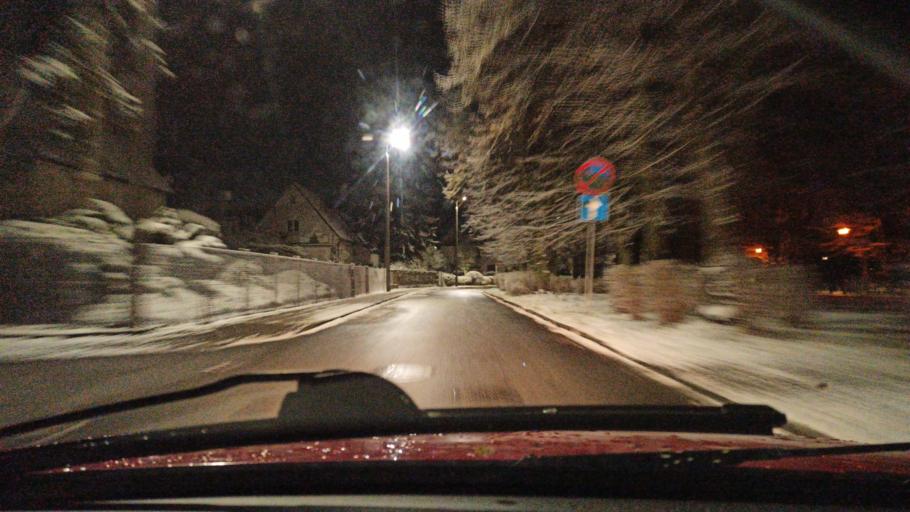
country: PL
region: Warmian-Masurian Voivodeship
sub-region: Powiat elblaski
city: Elblag
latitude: 54.1759
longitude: 19.4100
